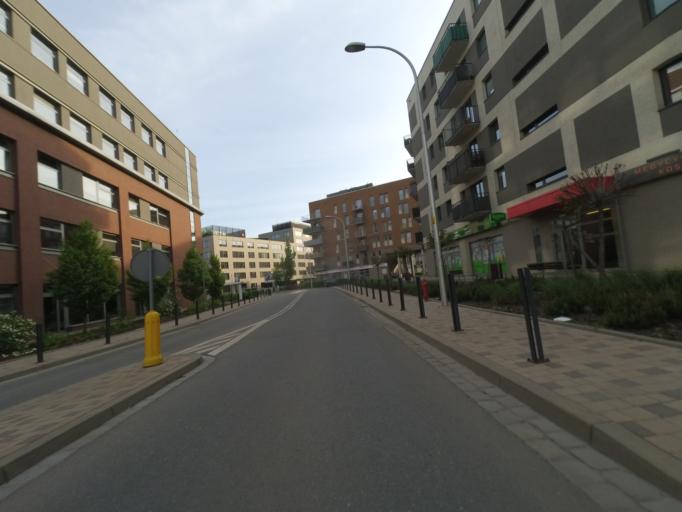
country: PL
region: Lower Silesian Voivodeship
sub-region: Powiat wroclawski
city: Wroclaw
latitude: 51.1296
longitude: 17.0453
